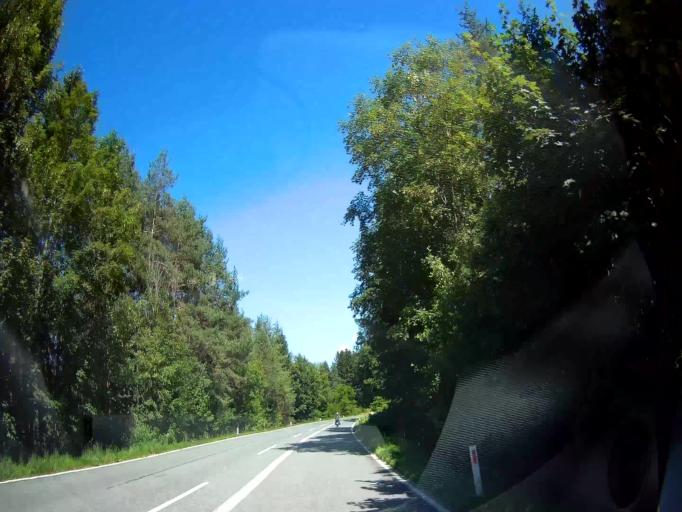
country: AT
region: Carinthia
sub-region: Politischer Bezirk Volkermarkt
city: Gallizien
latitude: 46.5516
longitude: 14.5067
